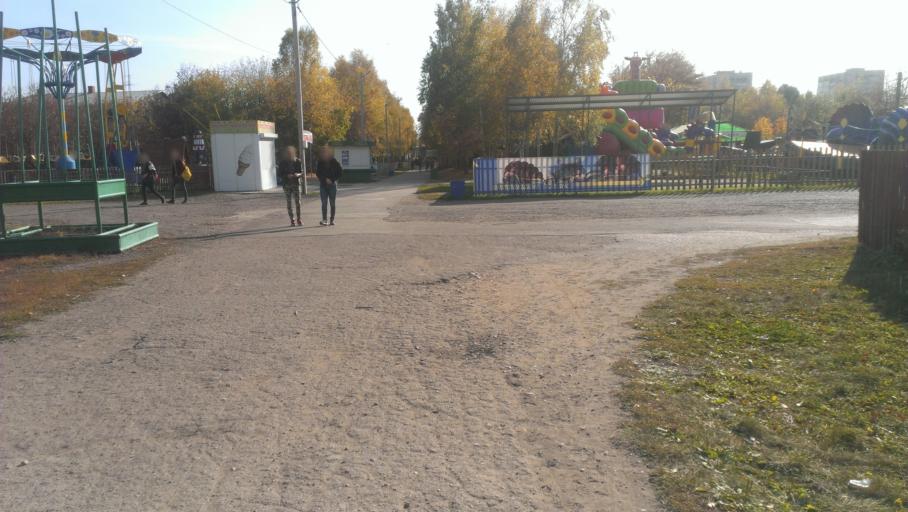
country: RU
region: Altai Krai
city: Novosilikatnyy
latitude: 53.3581
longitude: 83.6848
